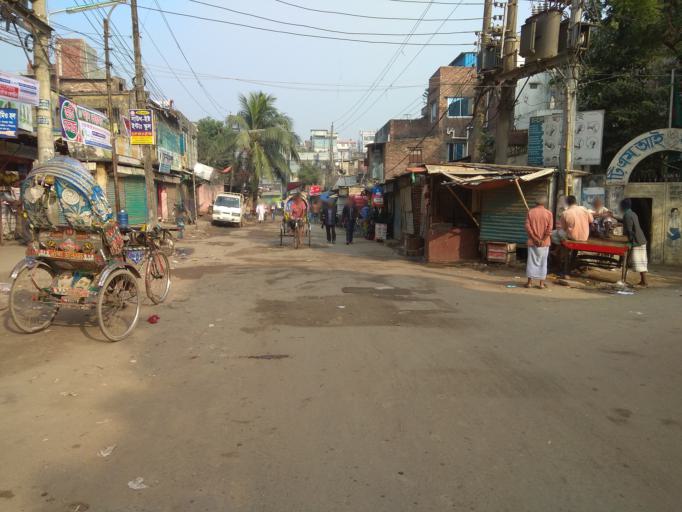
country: BD
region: Dhaka
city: Tungi
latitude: 23.8198
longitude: 90.3684
